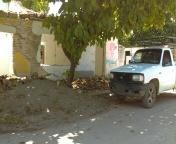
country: MX
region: Oaxaca
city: Asuncion Ixtaltepec
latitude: 16.5031
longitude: -95.0595
